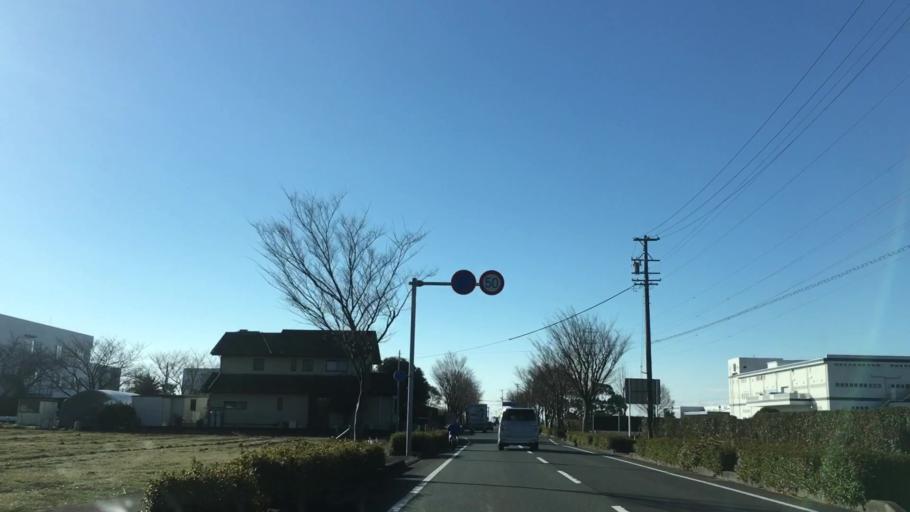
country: JP
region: Shizuoka
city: Hamakita
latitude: 34.8060
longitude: 137.7449
